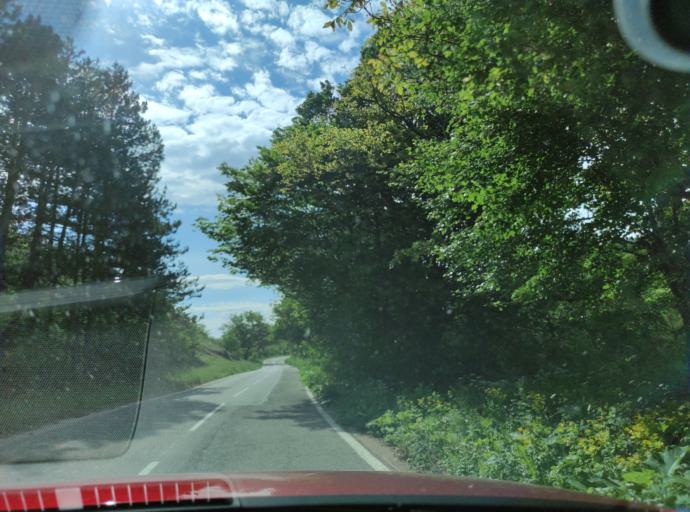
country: BG
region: Montana
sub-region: Obshtina Chiprovtsi
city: Chiprovtsi
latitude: 43.4862
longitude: 22.8163
